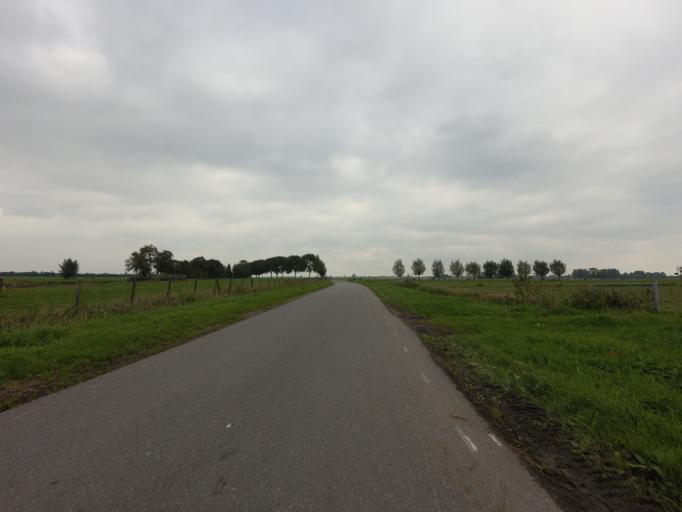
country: NL
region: South Holland
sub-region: Gemeente Sliedrecht
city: Sliedrecht
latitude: 51.8827
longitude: 4.7886
